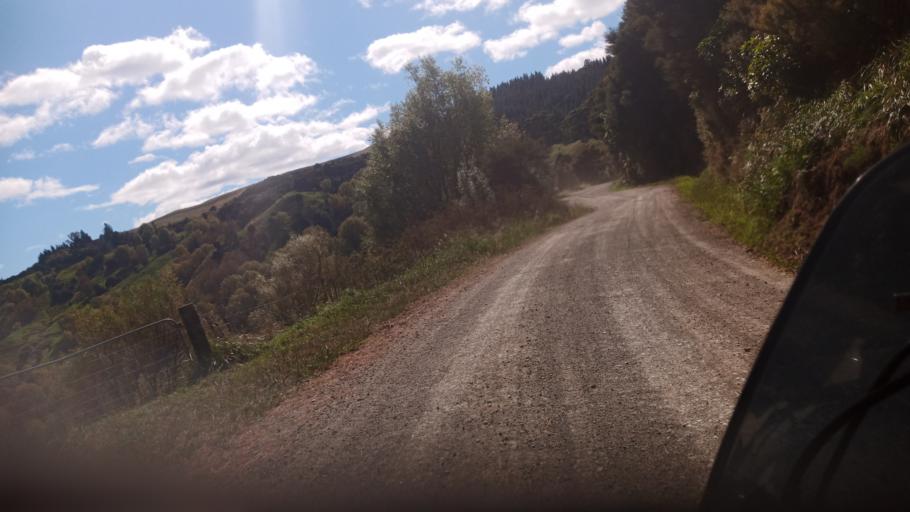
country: NZ
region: Gisborne
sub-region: Gisborne District
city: Gisborne
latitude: -38.4047
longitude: 177.6773
